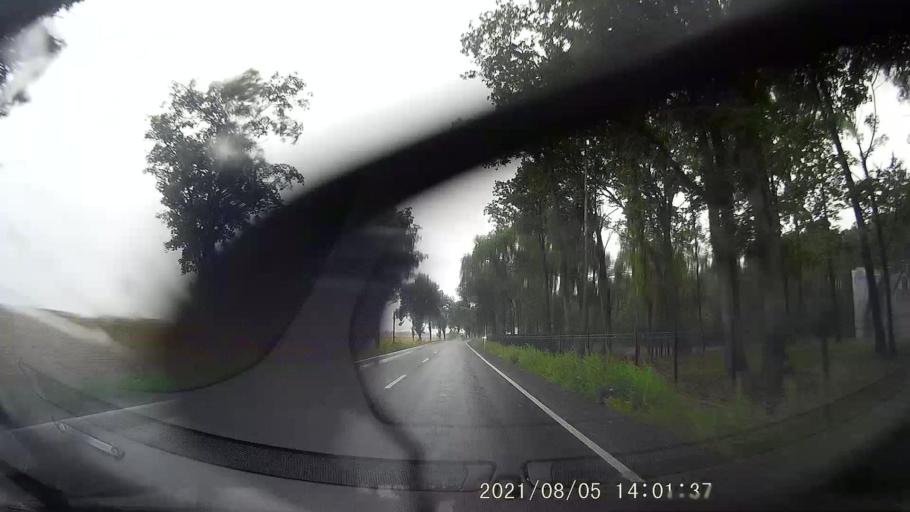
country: PL
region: Opole Voivodeship
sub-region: Powiat krapkowicki
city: Strzeleczki
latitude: 50.4490
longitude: 17.8903
